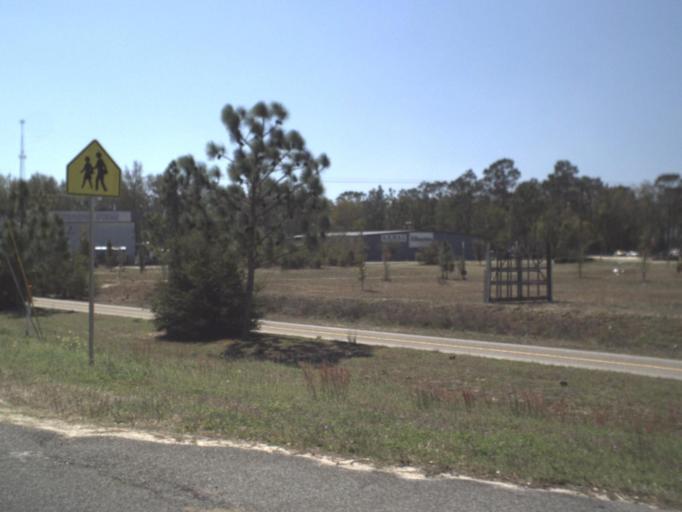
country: US
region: Florida
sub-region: Leon County
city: Tallahassee
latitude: 30.3827
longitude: -84.2733
